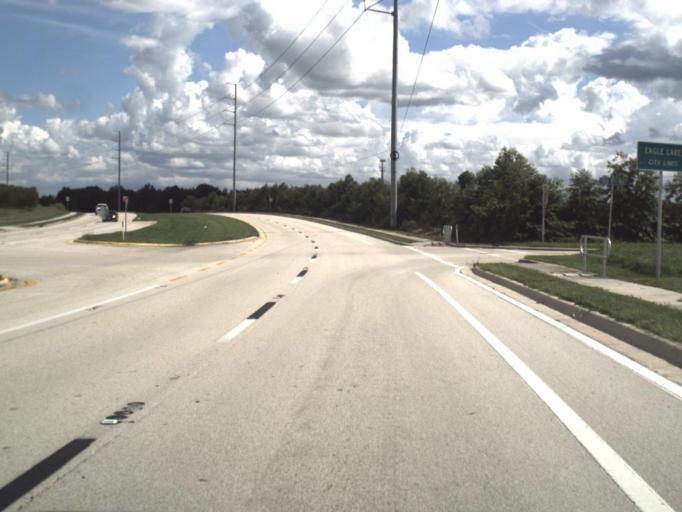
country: US
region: Florida
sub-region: Polk County
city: Eagle Lake
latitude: 27.9919
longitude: -81.7553
